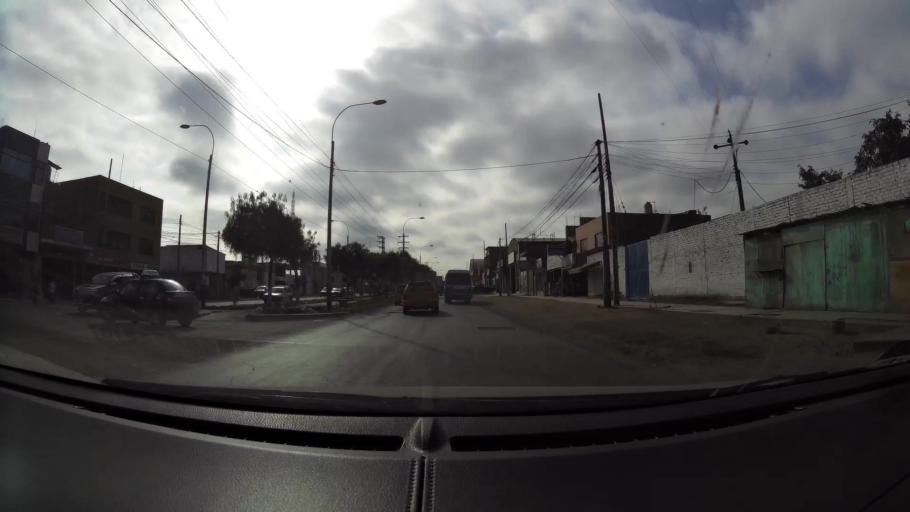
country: PE
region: La Libertad
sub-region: Provincia de Trujillo
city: La Esperanza
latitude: -8.0903
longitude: -79.0371
